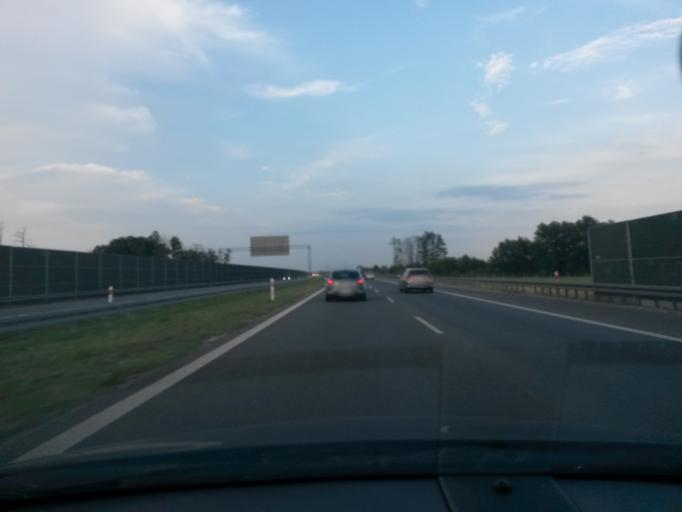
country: PL
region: Masovian Voivodeship
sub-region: Powiat grodziski
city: Milanowek
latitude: 52.1492
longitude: 20.6449
